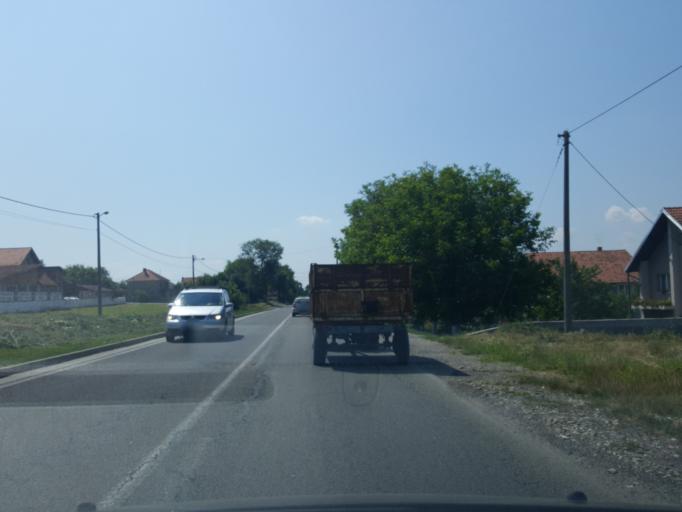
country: RS
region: Central Serbia
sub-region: Belgrade
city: Mladenovac
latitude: 44.4676
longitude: 20.6668
